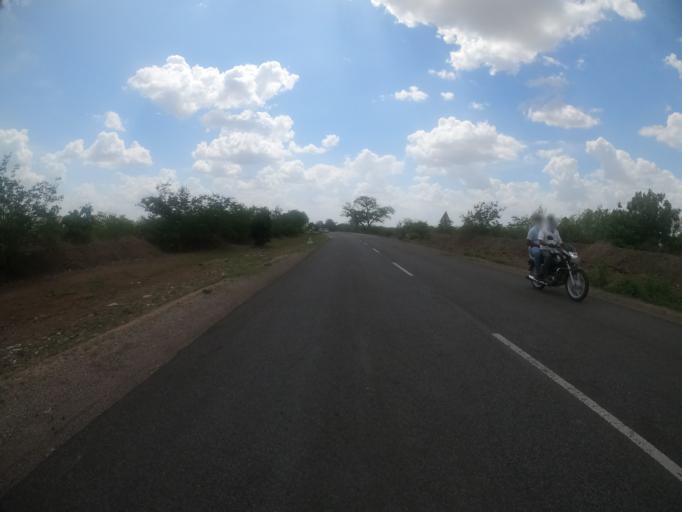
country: IN
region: Telangana
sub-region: Rangareddi
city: Sriramnagar
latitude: 17.3122
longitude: 78.1743
